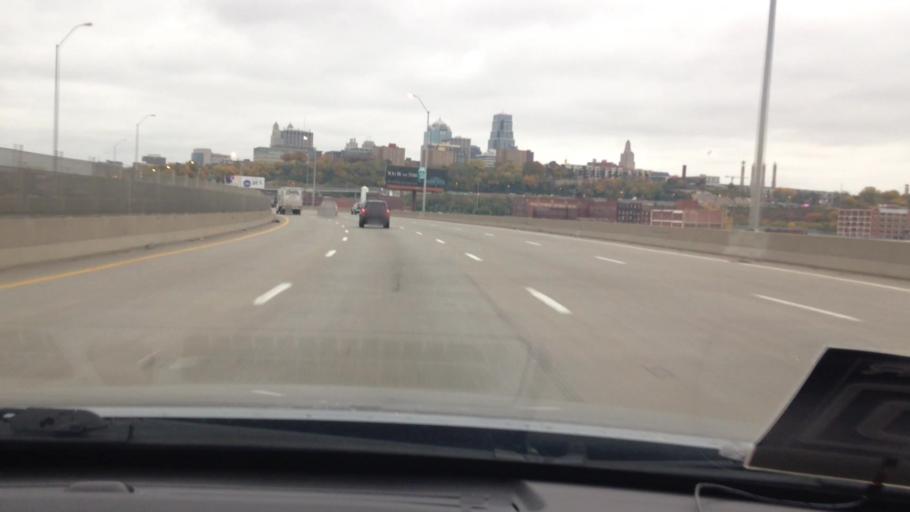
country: US
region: Kansas
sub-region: Wyandotte County
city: Kansas City
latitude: 39.1075
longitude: -94.6036
